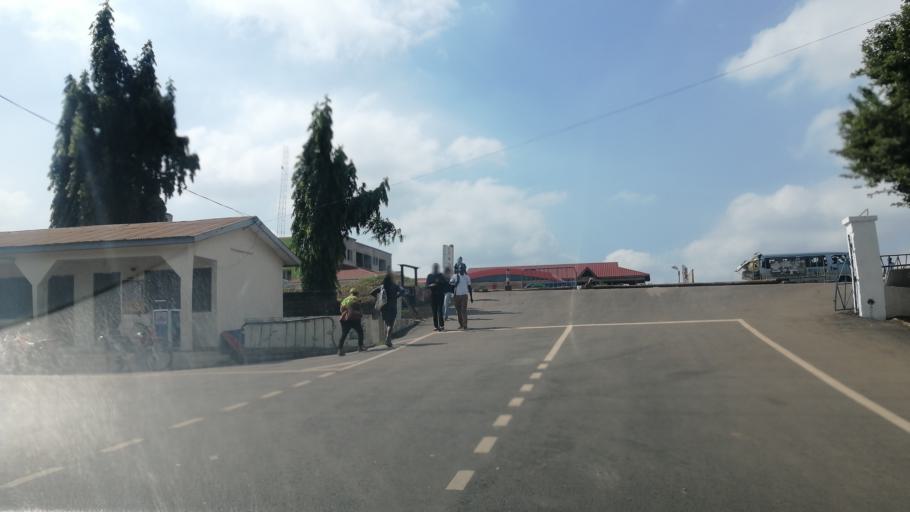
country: GH
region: Ashanti
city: Kumasi
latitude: 6.6970
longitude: -1.6823
